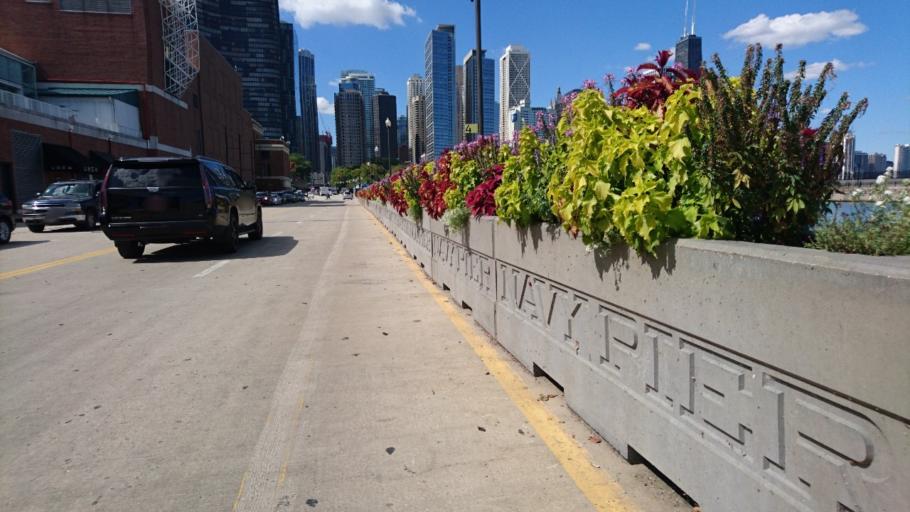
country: US
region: Illinois
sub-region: Cook County
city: Chicago
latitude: 41.8923
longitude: -87.6081
